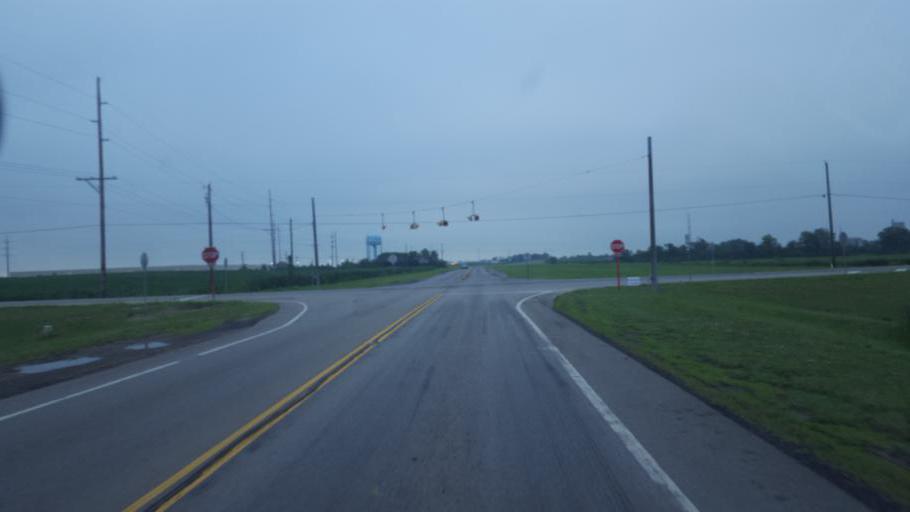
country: US
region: Ohio
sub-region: Fayette County
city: Washington Court House
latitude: 39.5425
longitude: -83.3970
